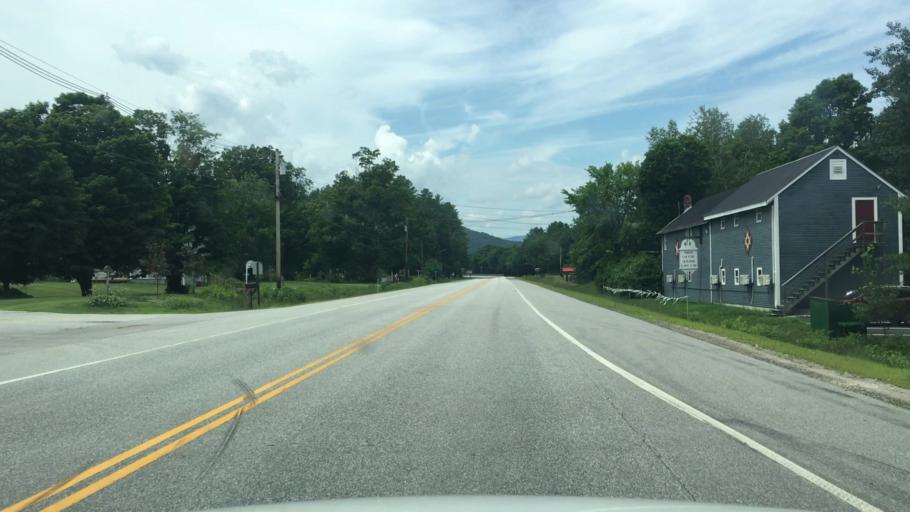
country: US
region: New Hampshire
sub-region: Grafton County
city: Rumney
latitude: 43.7949
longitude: -71.8174
